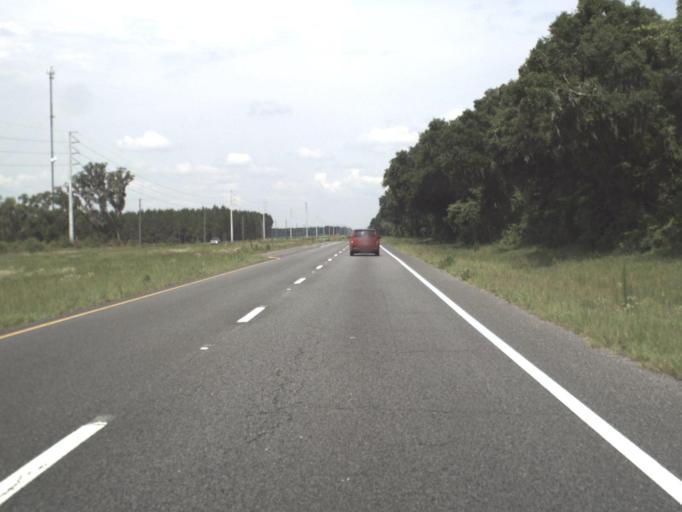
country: US
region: Florida
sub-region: Levy County
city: Chiefland
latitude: 29.4752
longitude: -82.7619
